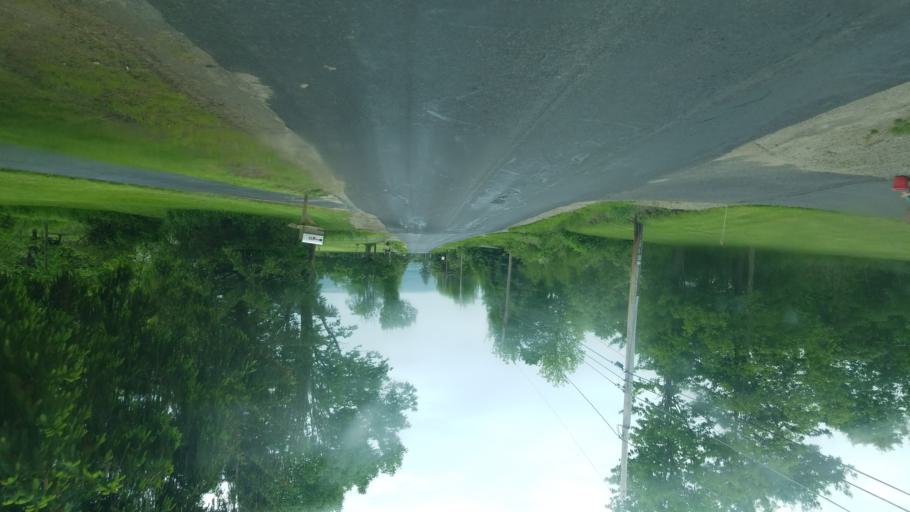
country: US
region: New York
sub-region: Herkimer County
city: Herkimer
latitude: 43.0424
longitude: -75.0114
